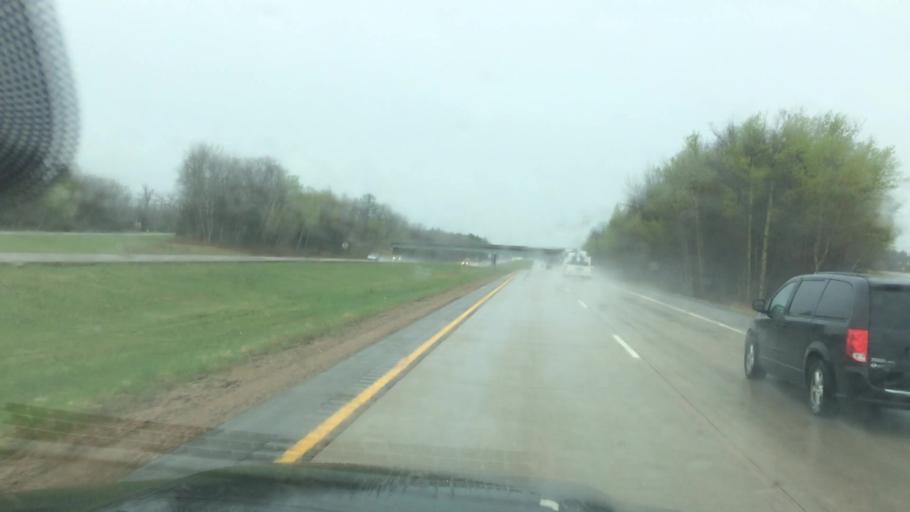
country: US
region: Wisconsin
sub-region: Marathon County
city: Mosinee
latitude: 44.6787
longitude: -89.6419
